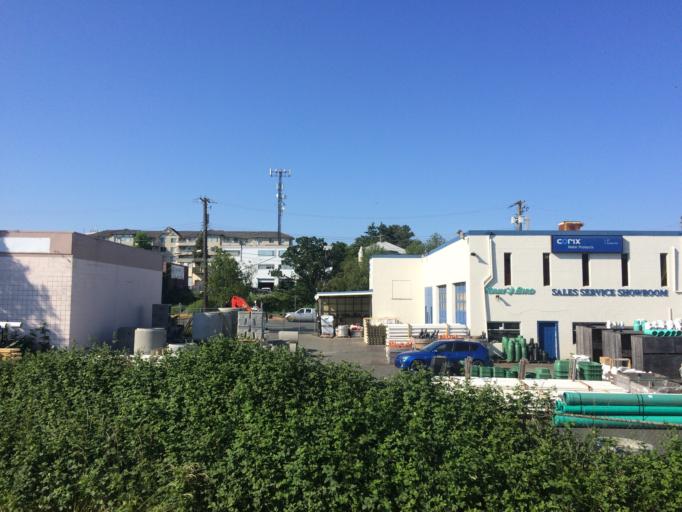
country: CA
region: British Columbia
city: Victoria
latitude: 48.4556
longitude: -123.3788
